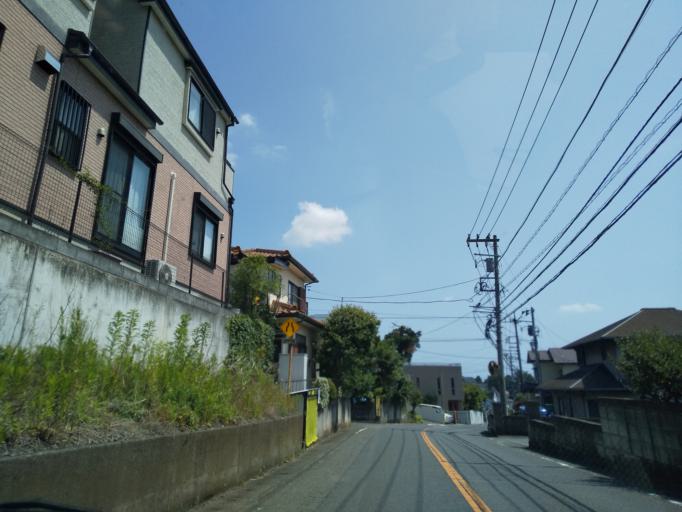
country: JP
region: Kanagawa
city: Zama
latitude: 35.5102
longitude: 139.3912
